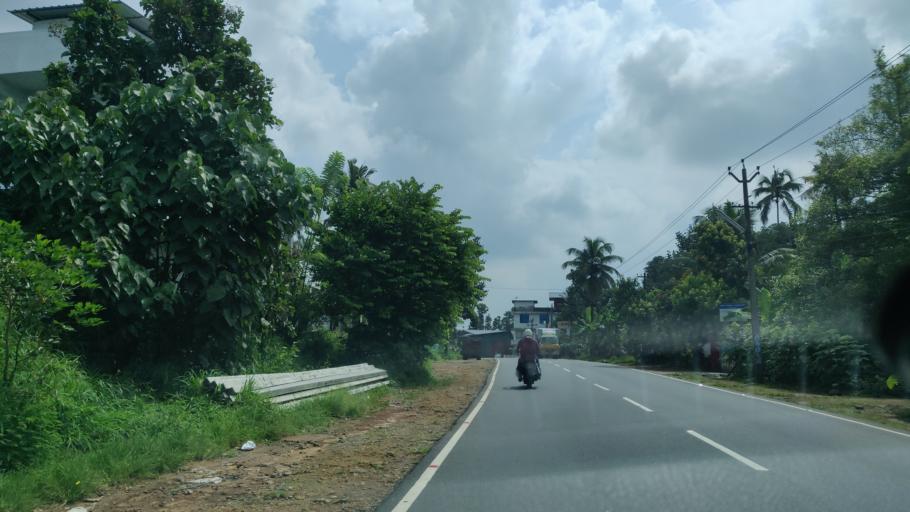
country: IN
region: Kerala
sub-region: Ernakulam
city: Angamali
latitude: 10.1691
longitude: 76.4232
